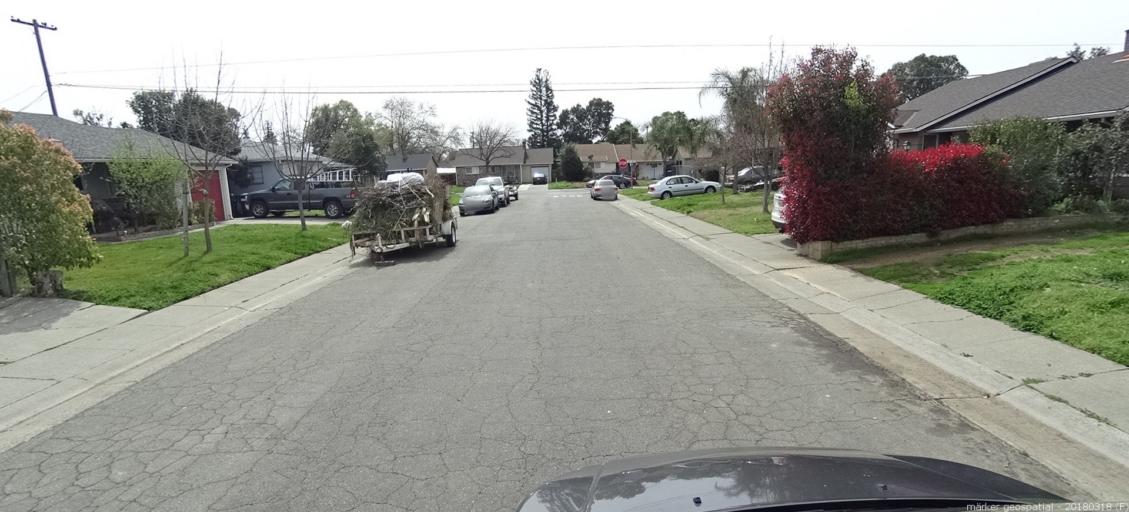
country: US
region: California
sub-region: Sacramento County
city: Parkway
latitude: 38.5165
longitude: -121.4572
